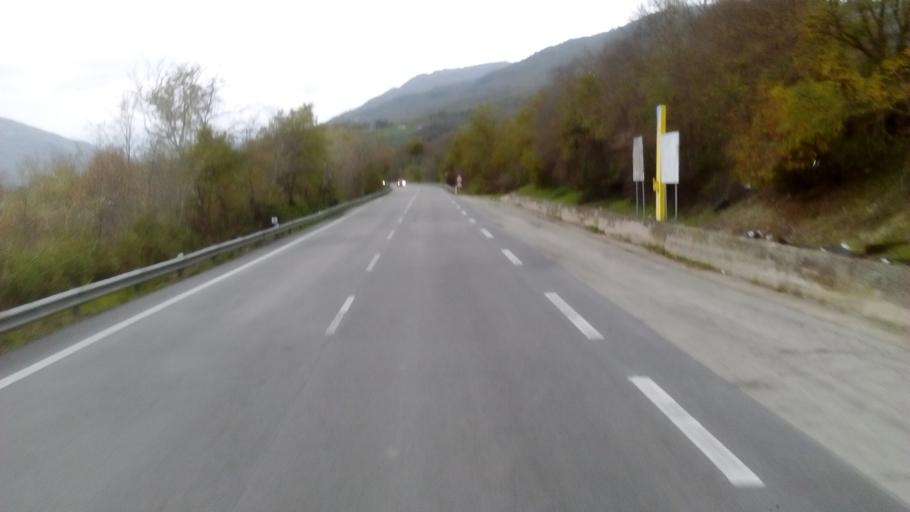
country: IT
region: Abruzzo
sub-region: Provincia di Chieti
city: Celenza sul Trigno
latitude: 41.8873
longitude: 14.6088
